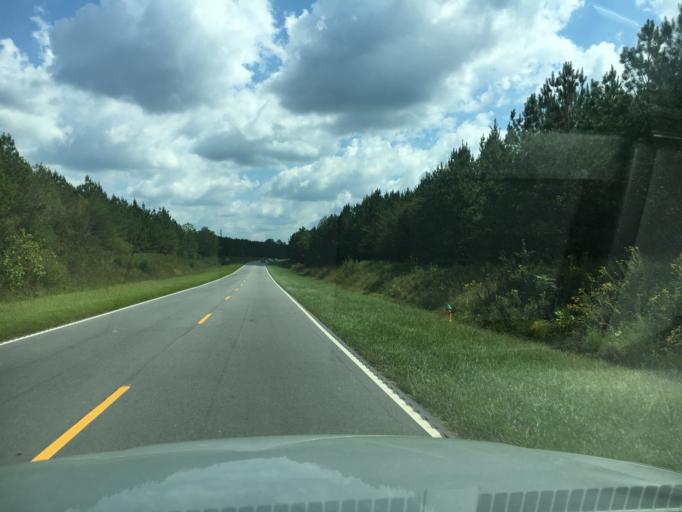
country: US
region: South Carolina
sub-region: Greenwood County
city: Greenwood
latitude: 34.1527
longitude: -82.1634
